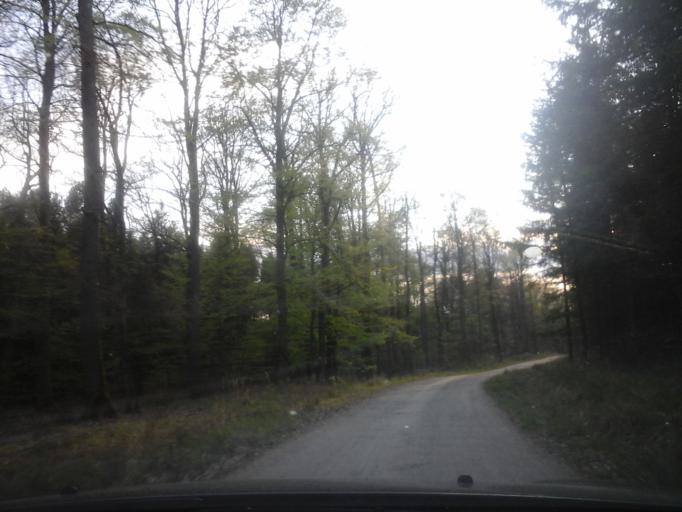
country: PL
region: West Pomeranian Voivodeship
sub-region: Powiat choszczenski
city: Krzecin
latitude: 52.9941
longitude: 15.4744
